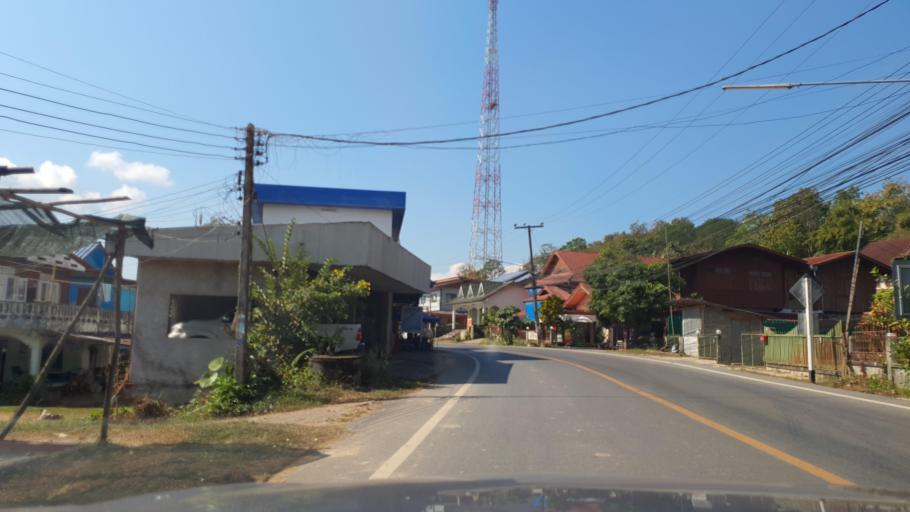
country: TH
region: Nan
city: Tha Wang Pha
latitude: 19.0822
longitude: 100.8793
